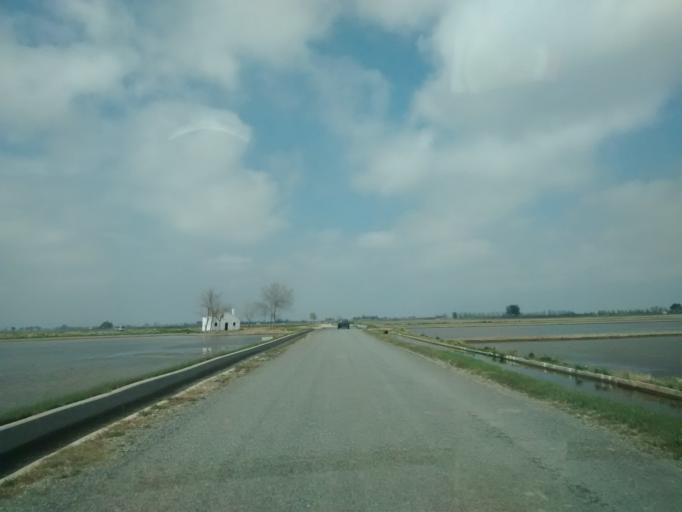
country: ES
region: Catalonia
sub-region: Provincia de Tarragona
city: Deltebre
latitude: 40.6818
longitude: 0.7958
